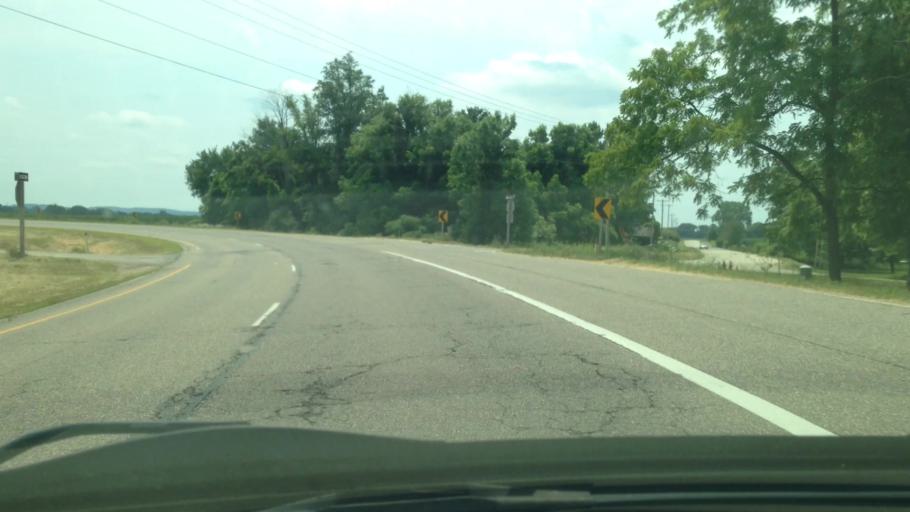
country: US
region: Wisconsin
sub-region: Sauk County
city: Prairie du Sac
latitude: 43.3522
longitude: -89.7679
